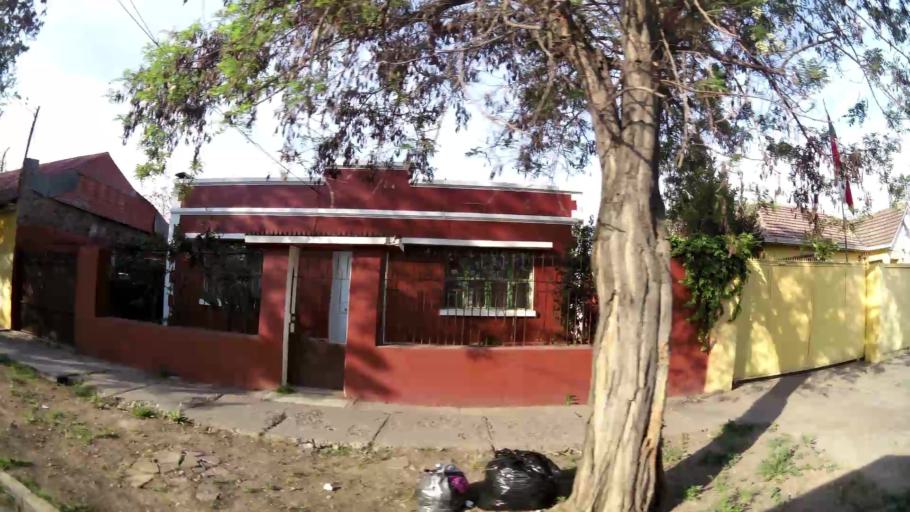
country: CL
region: Santiago Metropolitan
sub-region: Provincia de Santiago
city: Santiago
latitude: -33.5161
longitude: -70.6656
